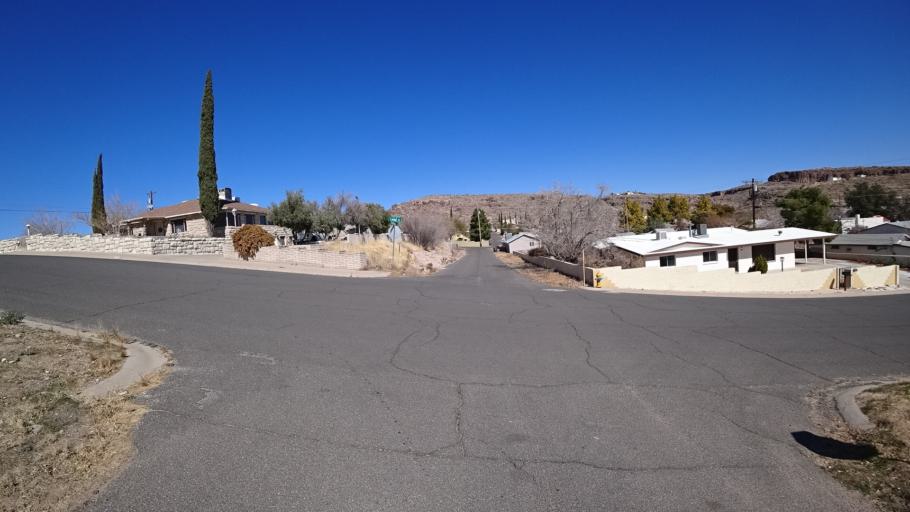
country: US
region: Arizona
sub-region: Mohave County
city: Kingman
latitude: 35.1965
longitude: -114.0623
